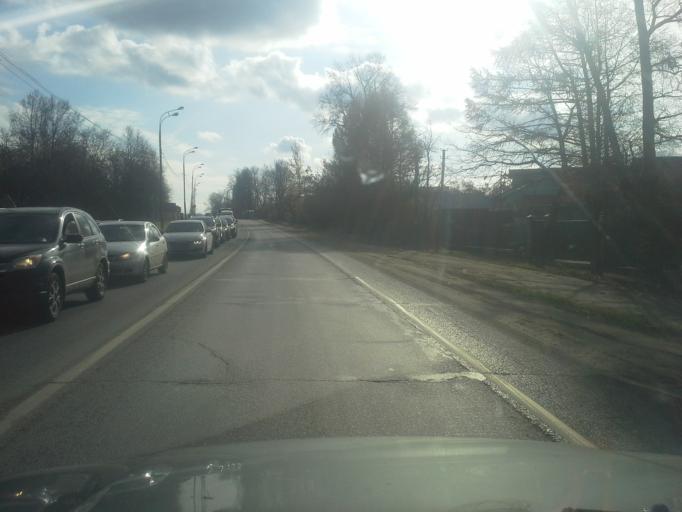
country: RU
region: Moskovskaya
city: Zvenigorod
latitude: 55.6991
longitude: 36.8840
